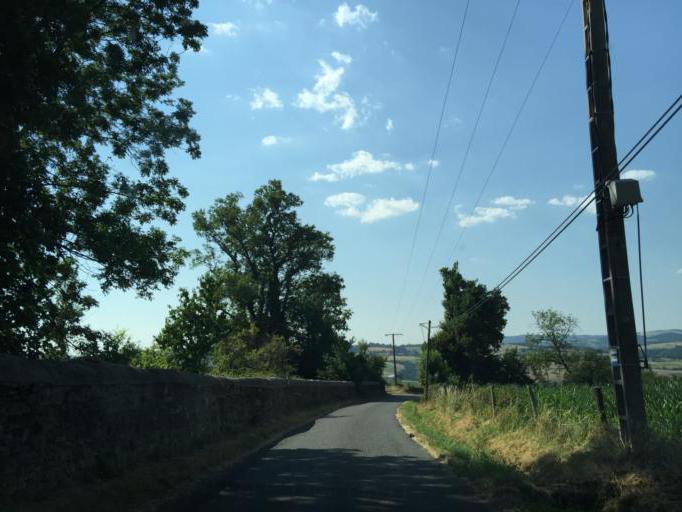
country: FR
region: Rhone-Alpes
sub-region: Departement de la Loire
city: Saint-Jean-Bonnefonds
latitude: 45.4465
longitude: 4.4915
